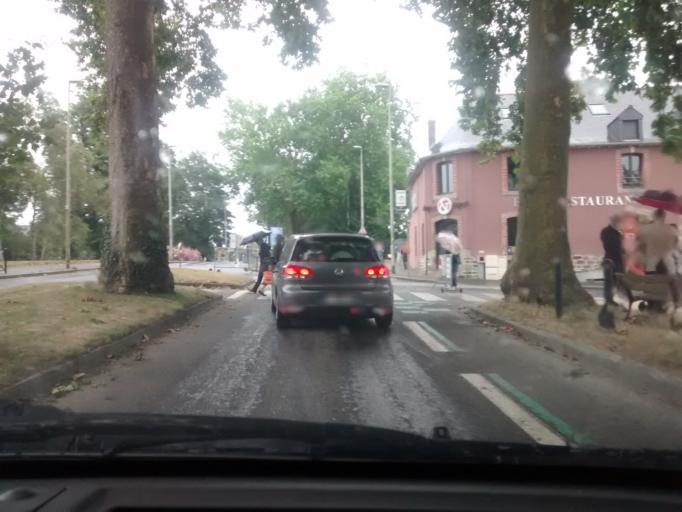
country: FR
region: Brittany
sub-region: Departement d'Ille-et-Vilaine
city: Betton
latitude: 48.1818
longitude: -1.6408
